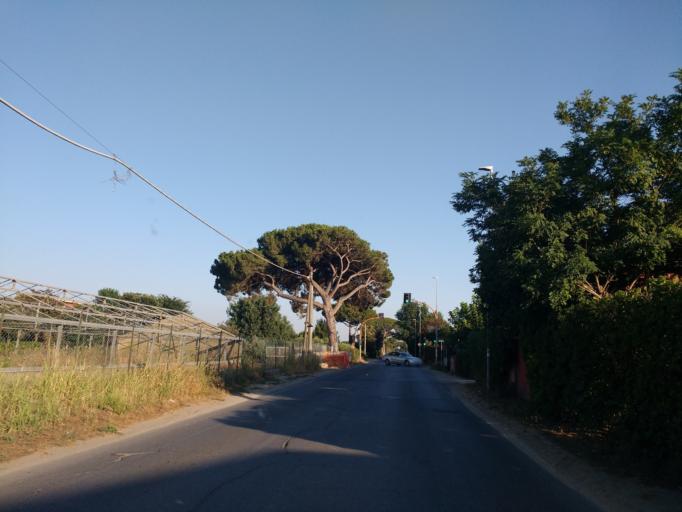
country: IT
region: Latium
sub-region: Citta metropolitana di Roma Capitale
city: Focene
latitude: 41.8413
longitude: 12.2255
